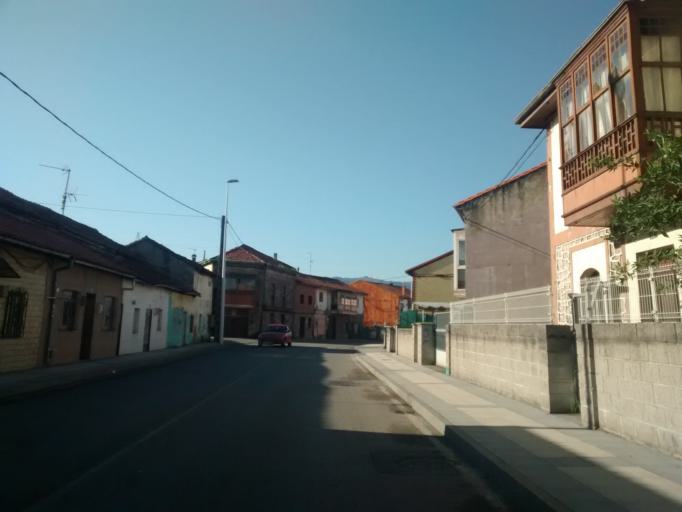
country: ES
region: Cantabria
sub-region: Provincia de Cantabria
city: Torrelavega
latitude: 43.3407
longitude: -4.0586
